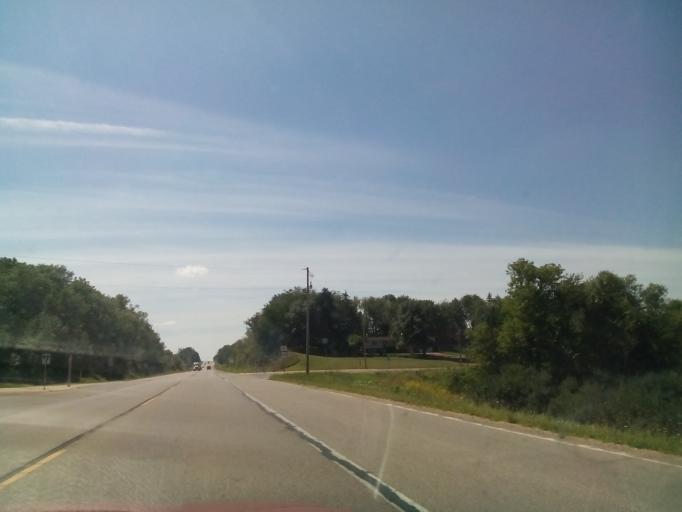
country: US
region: Wisconsin
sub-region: Green County
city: Monticello
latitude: 42.7428
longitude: -89.5992
